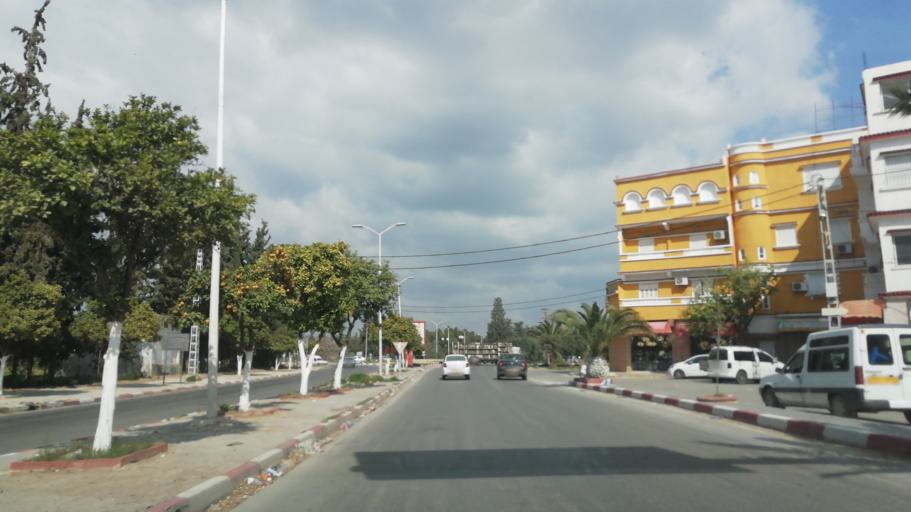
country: DZ
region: Mascara
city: Mascara
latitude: 35.5971
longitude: 0.0790
